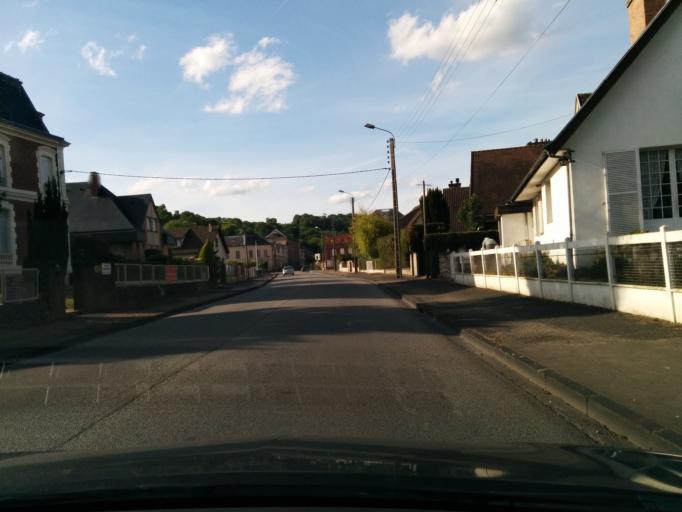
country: FR
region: Haute-Normandie
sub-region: Departement de l'Eure
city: Les Andelys
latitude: 49.2465
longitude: 1.4138
